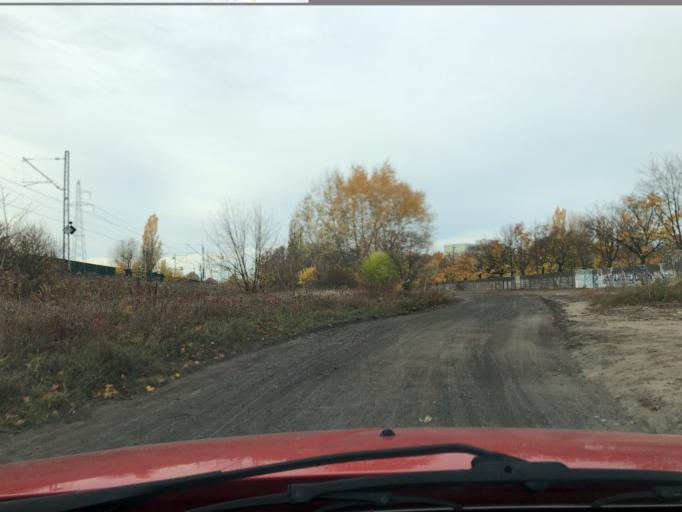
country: PL
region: Greater Poland Voivodeship
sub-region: Powiat poznanski
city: Plewiska
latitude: 52.3788
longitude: 16.8428
